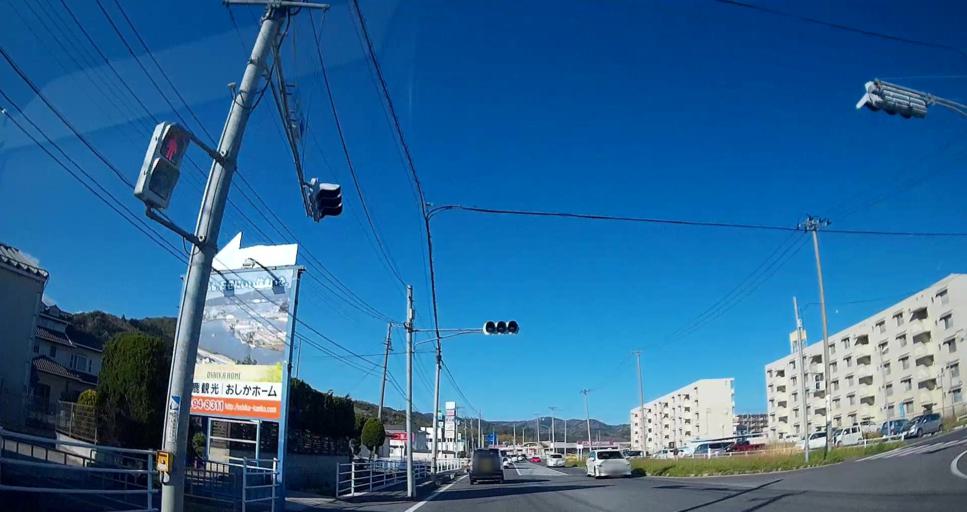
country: JP
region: Miyagi
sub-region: Oshika Gun
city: Onagawa Cho
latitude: 38.4262
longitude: 141.3719
